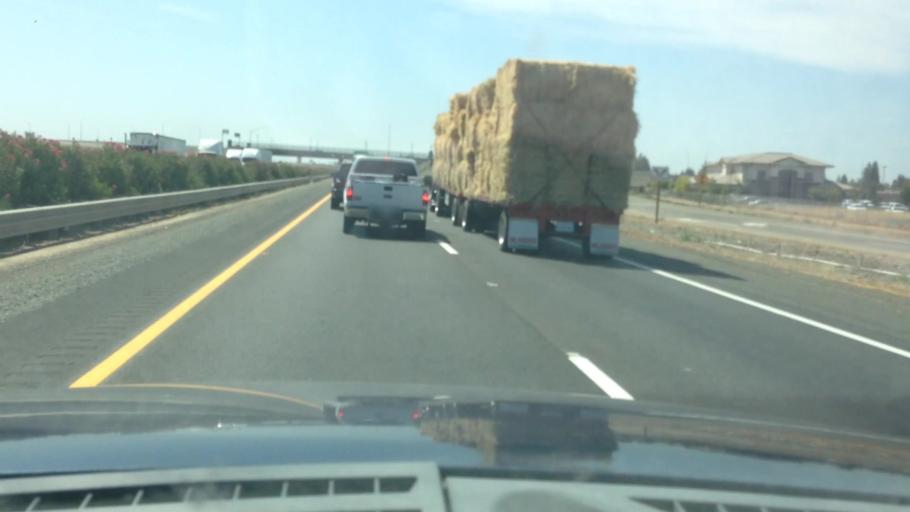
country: US
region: California
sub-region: Tulare County
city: Tulare
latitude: 36.2416
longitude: -119.3455
